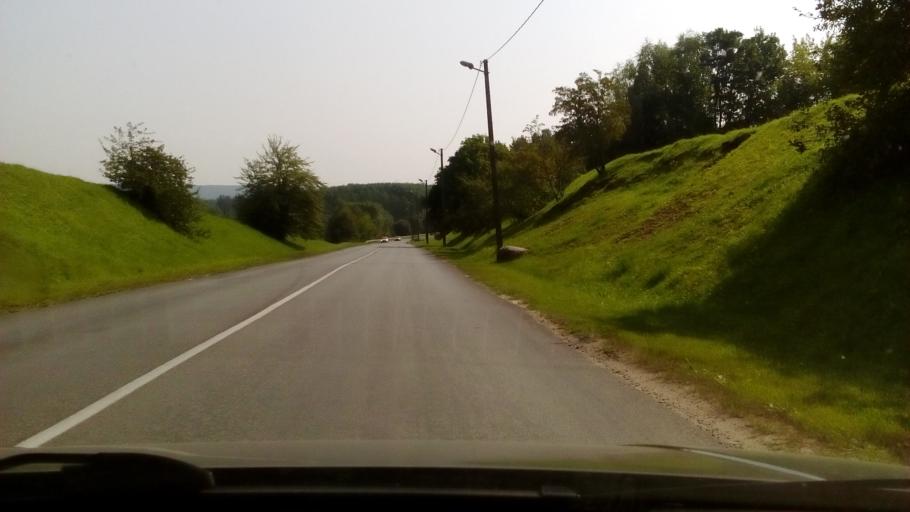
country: LT
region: Alytaus apskritis
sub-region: Alytus
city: Alytus
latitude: 54.4093
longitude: 24.0275
